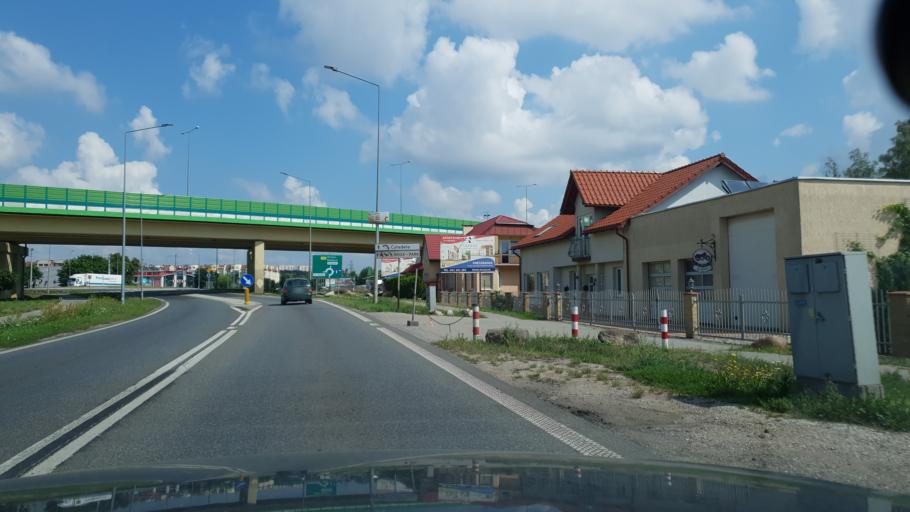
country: PL
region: Kujawsko-Pomorskie
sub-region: Grudziadz
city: Grudziadz
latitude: 53.4453
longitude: 18.7283
